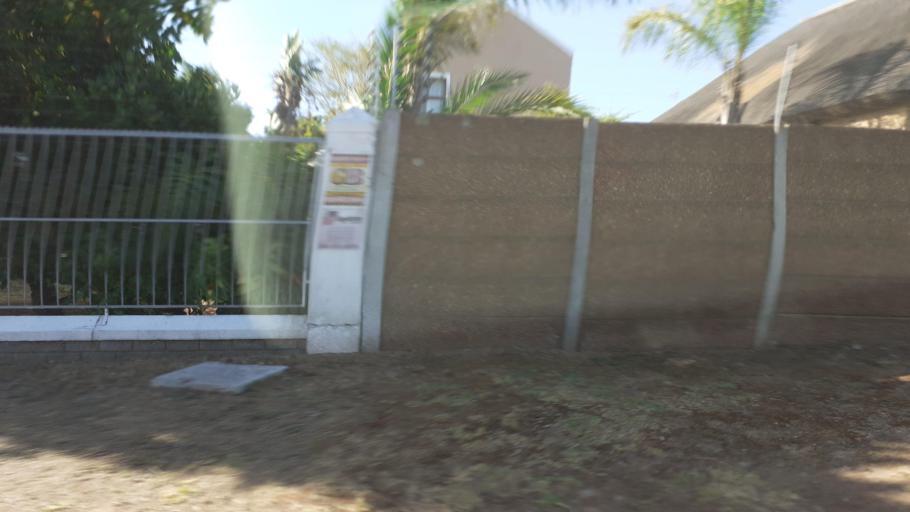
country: ZA
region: Western Cape
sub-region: City of Cape Town
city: Kraaifontein
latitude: -33.8242
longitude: 18.6773
